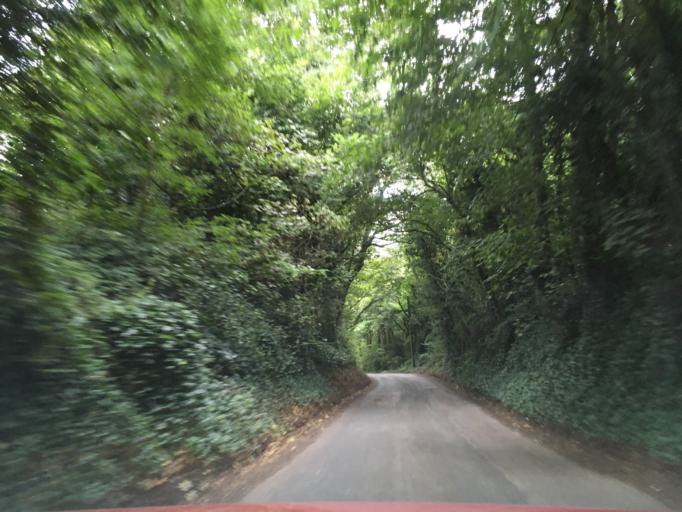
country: GB
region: England
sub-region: South Gloucestershire
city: Alveston
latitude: 51.5818
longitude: -2.5384
